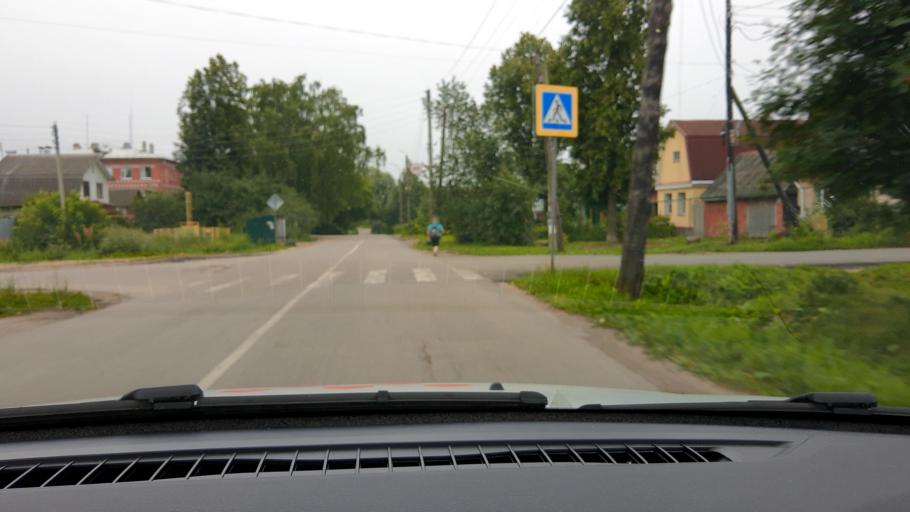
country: RU
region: Nizjnij Novgorod
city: Bogorodsk
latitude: 56.0961
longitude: 43.5101
